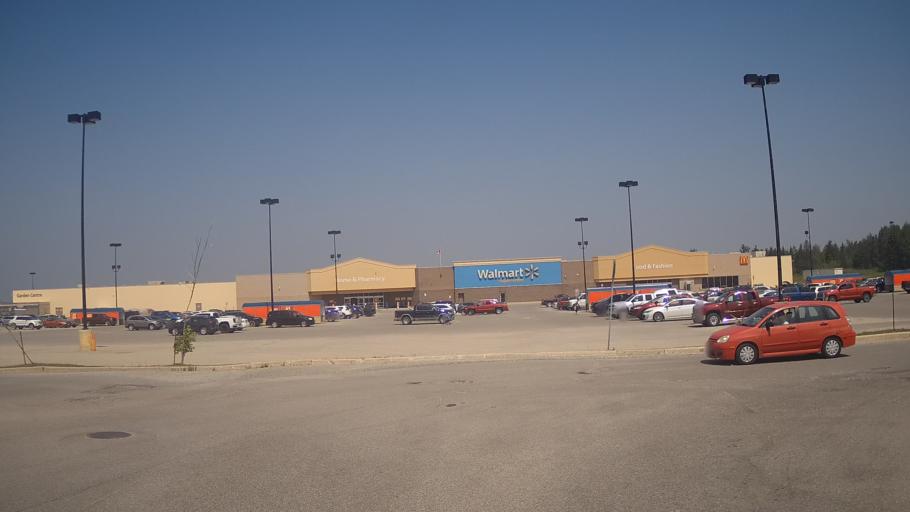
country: CA
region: Ontario
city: Timmins
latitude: 48.4731
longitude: -81.3933
